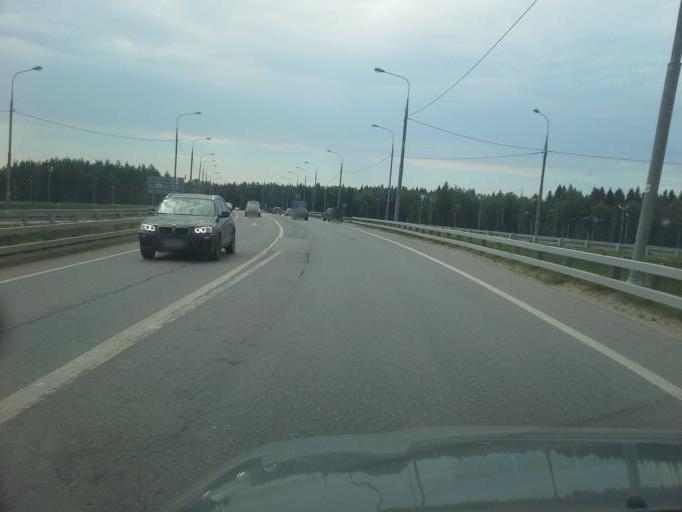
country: RU
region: Moskovskaya
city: Kokoshkino
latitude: 55.5586
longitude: 37.1497
